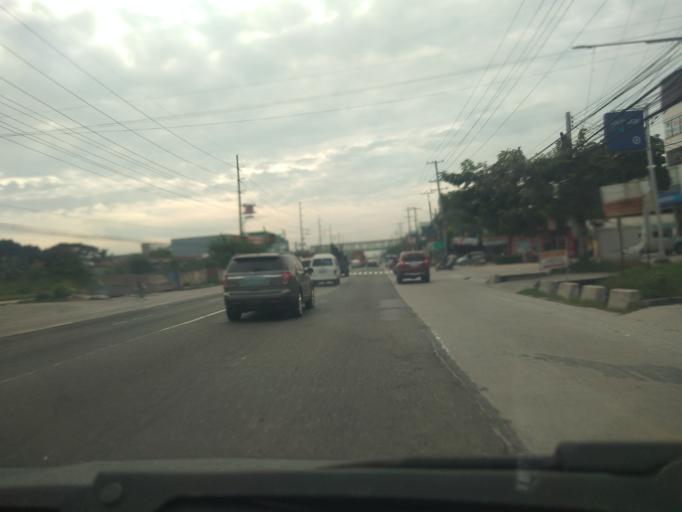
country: PH
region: Central Luzon
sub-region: Province of Pampanga
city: Bulaon
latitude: 15.0638
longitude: 120.6528
